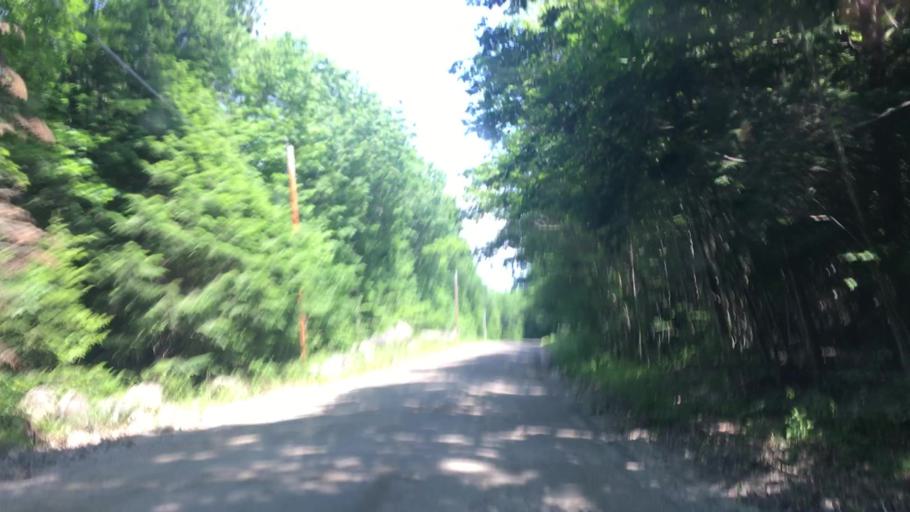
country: US
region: Maine
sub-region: Kennebec County
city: Monmouth
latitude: 44.2905
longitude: -70.0554
